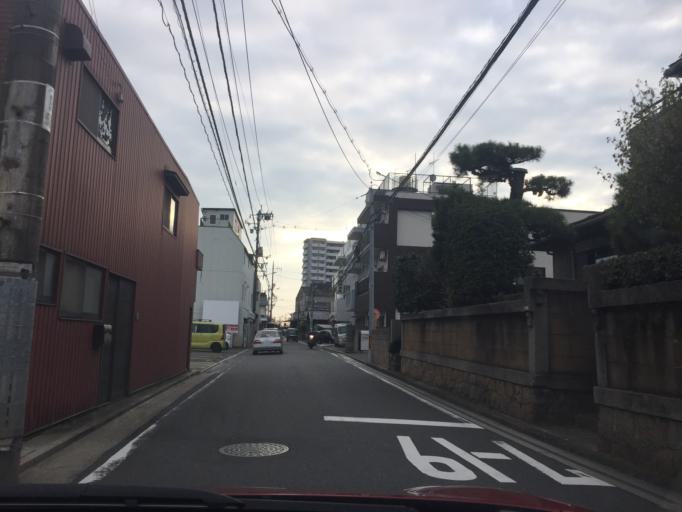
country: JP
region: Hiroshima
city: Hiroshima-shi
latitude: 34.4283
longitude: 132.4577
